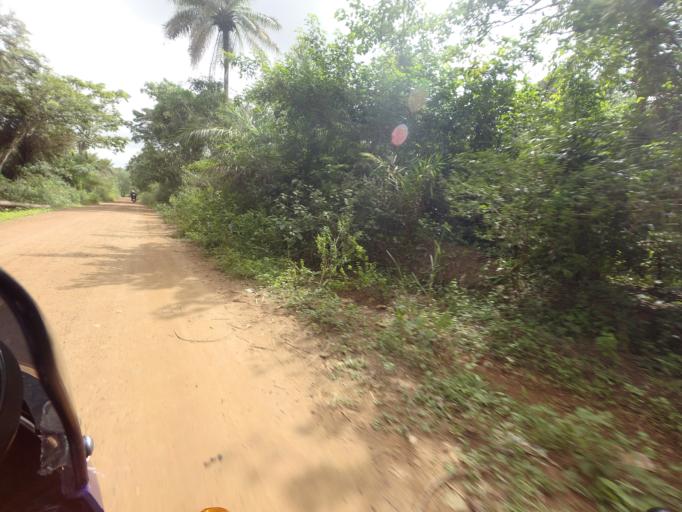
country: SL
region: Northern Province
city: Kambia
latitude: 9.1151
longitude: -12.9484
